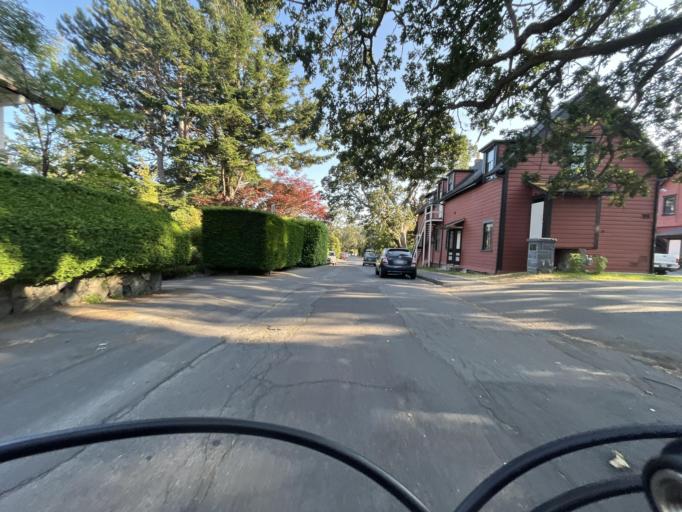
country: CA
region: British Columbia
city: Victoria
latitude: 48.4213
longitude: -123.3444
